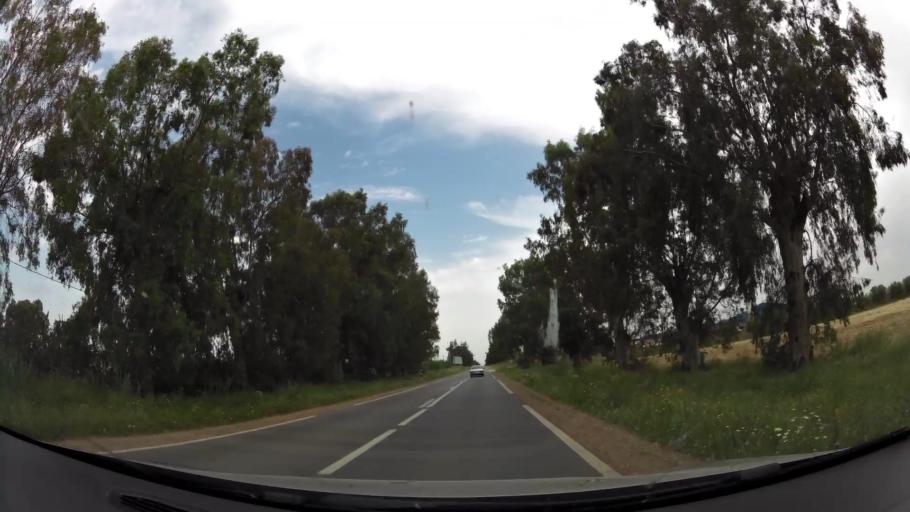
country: MA
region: Rabat-Sale-Zemmour-Zaer
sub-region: Khemisset
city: Tiflet
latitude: 33.8682
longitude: -6.2754
